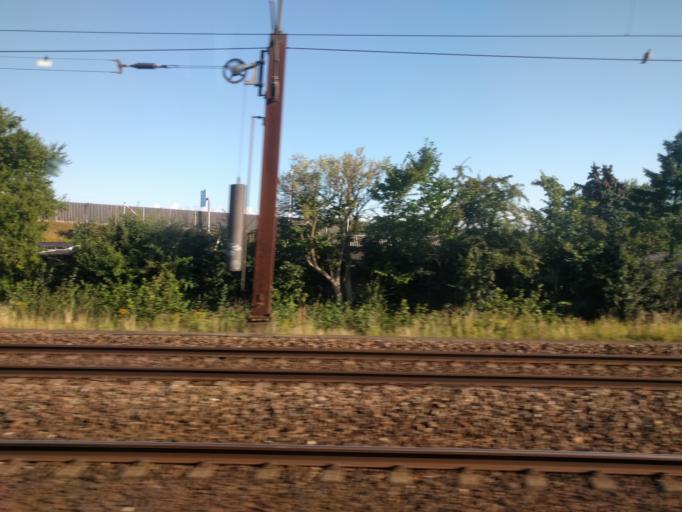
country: DK
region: Zealand
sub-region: Roskilde Kommune
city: Vindinge
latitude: 55.6486
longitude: 12.1460
